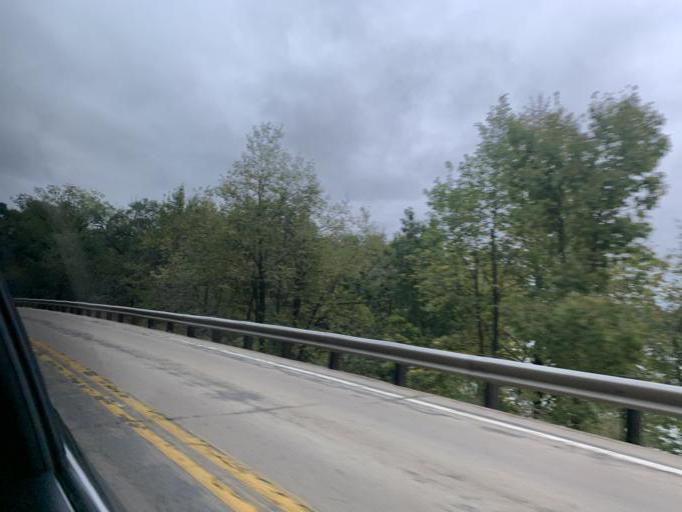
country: US
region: Wisconsin
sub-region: Grant County
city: Muscoda
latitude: 43.2114
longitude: -90.3349
